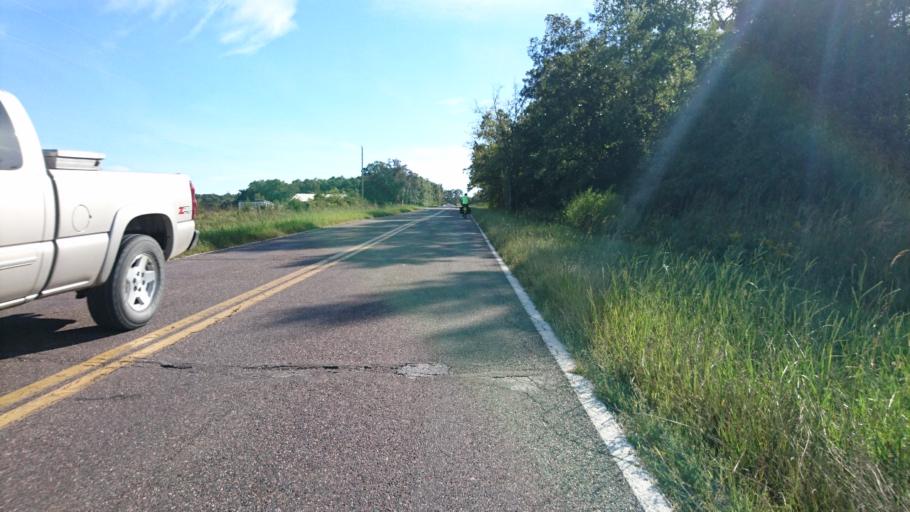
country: US
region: Missouri
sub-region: Crawford County
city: Bourbon
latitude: 38.1221
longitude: -91.3095
